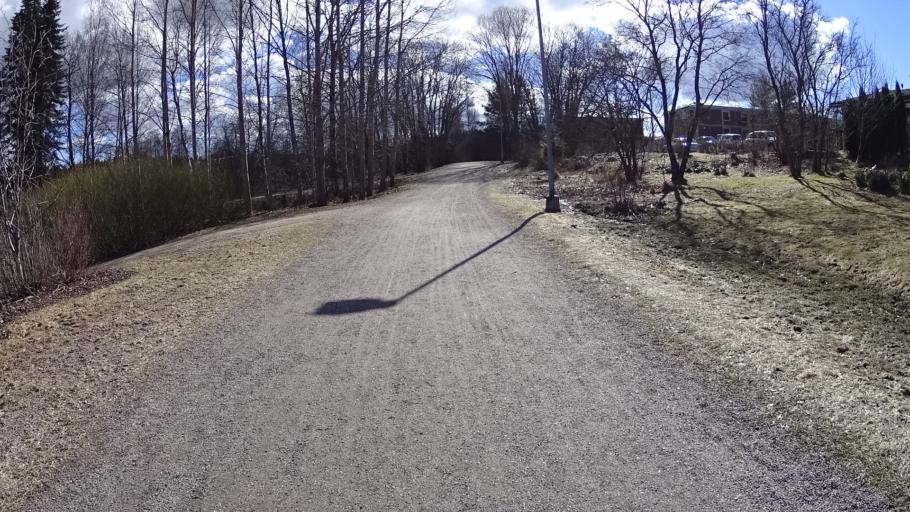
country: FI
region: Uusimaa
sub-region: Helsinki
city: Kauniainen
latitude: 60.2345
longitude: 24.7264
